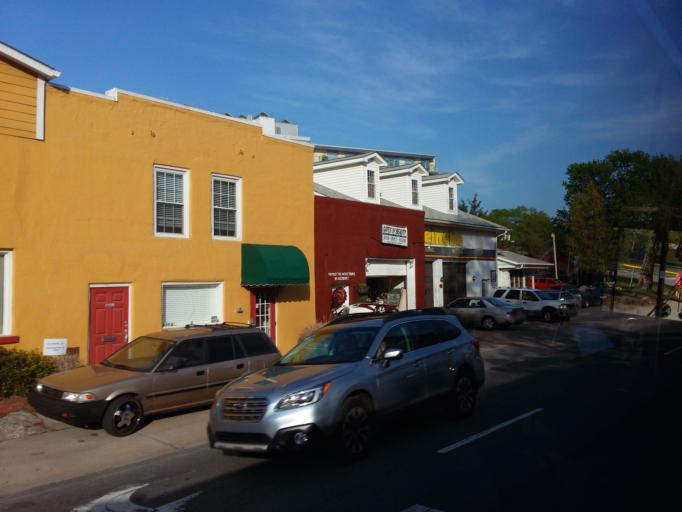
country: US
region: North Carolina
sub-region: Orange County
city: Carrboro
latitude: 35.9105
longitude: -79.0666
